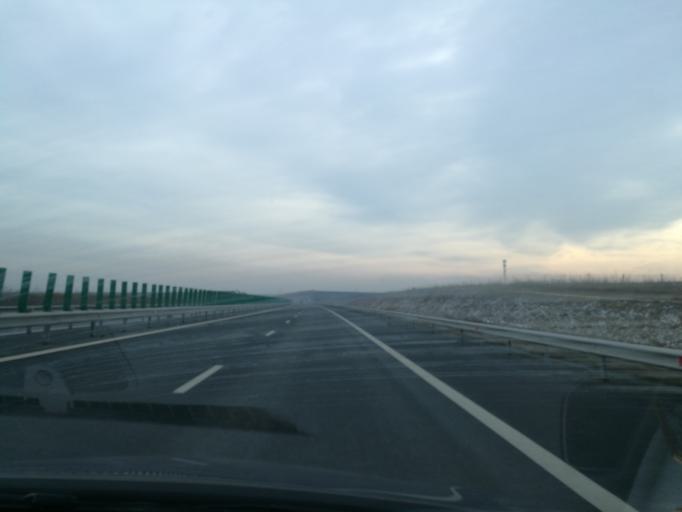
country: RO
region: Constanta
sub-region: Comuna Saligny
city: Saligny
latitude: 44.2458
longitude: 28.0867
